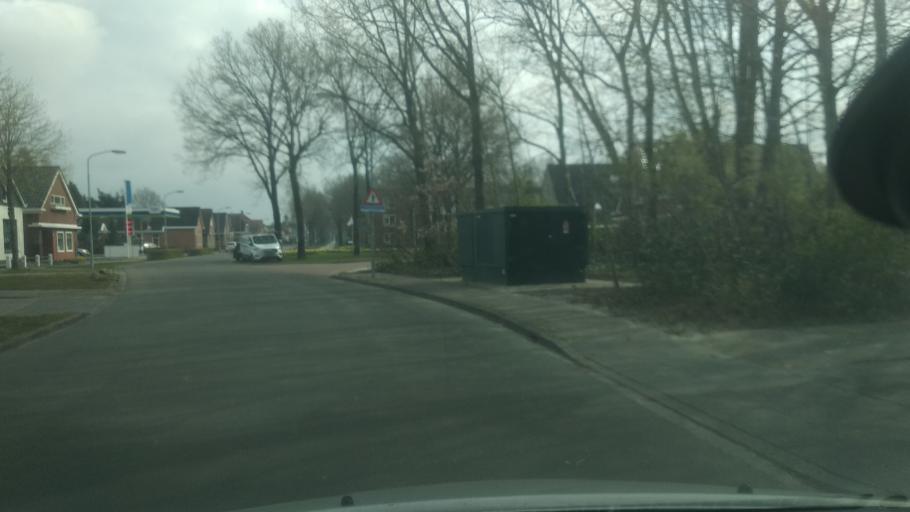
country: NL
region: Groningen
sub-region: Gemeente Stadskanaal
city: Stadskanaal
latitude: 52.9013
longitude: 6.9171
